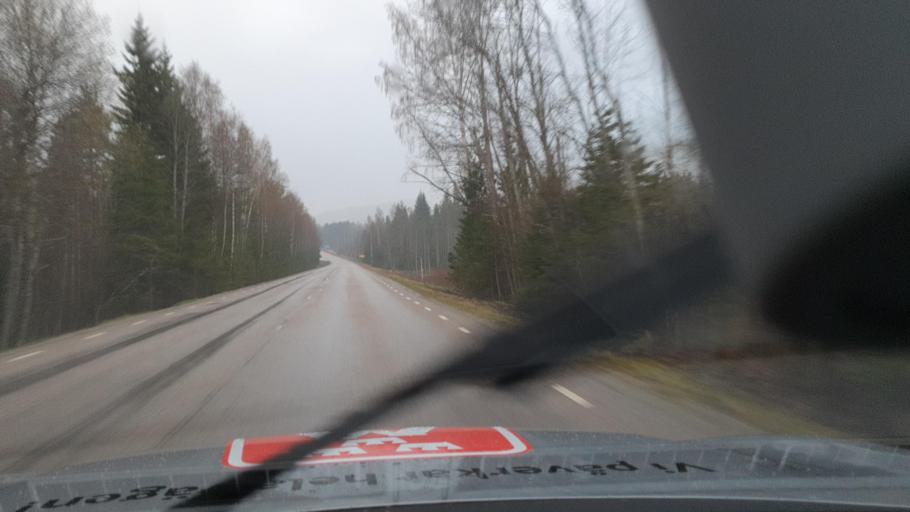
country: SE
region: Vaesternorrland
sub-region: OErnskoeldsviks Kommun
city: Bjasta
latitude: 63.2153
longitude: 18.4769
